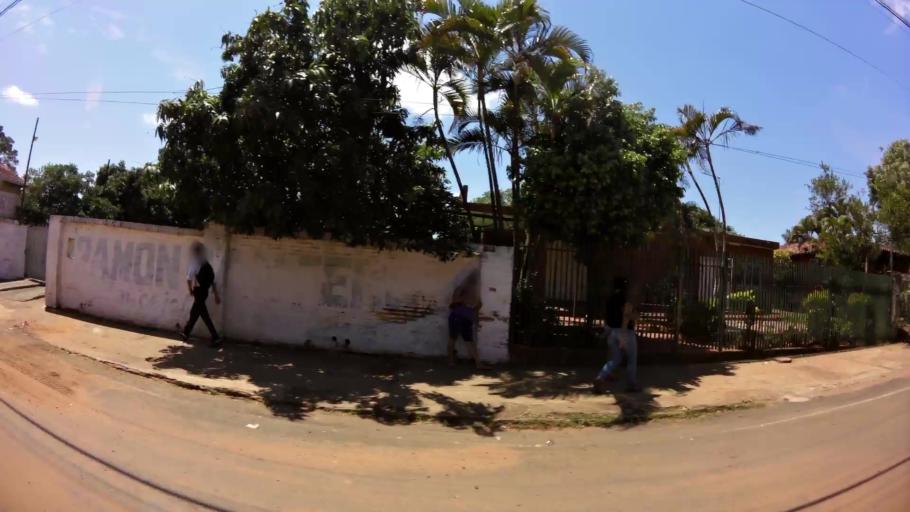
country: PY
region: Central
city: Nemby
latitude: -25.4057
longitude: -57.5268
